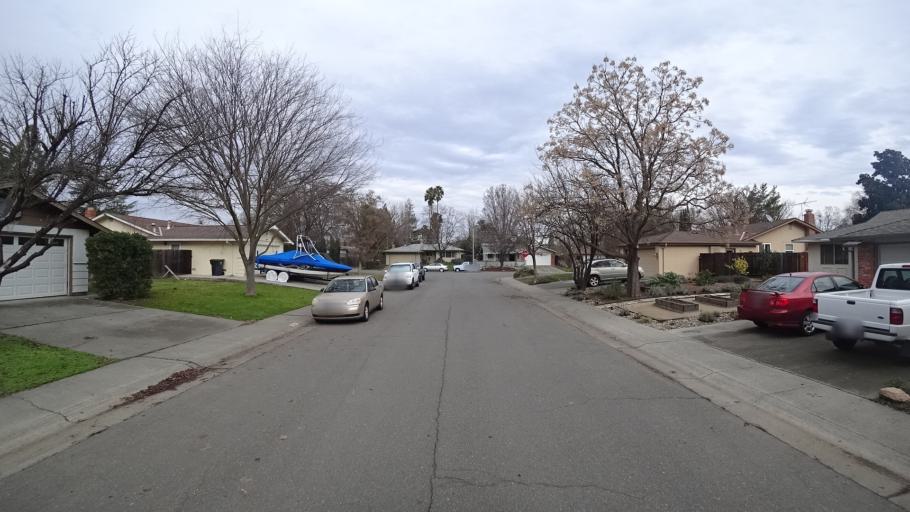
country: US
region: California
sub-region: Yolo County
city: Davis
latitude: 38.5594
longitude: -121.7238
